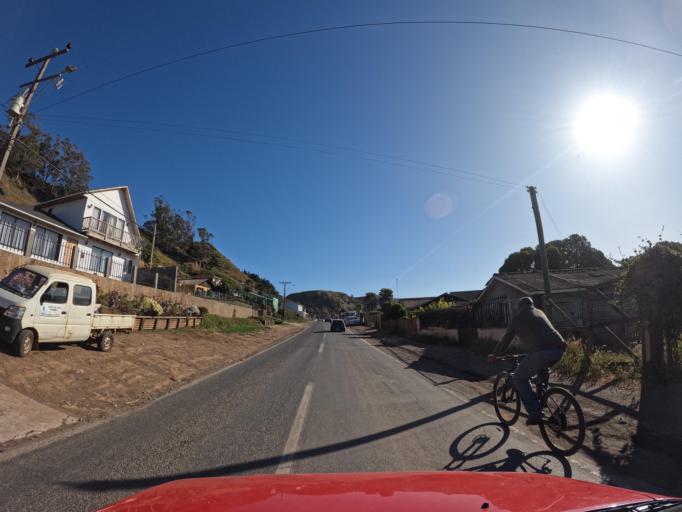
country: CL
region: Maule
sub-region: Provincia de Talca
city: Constitucion
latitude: -34.8824
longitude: -72.1578
